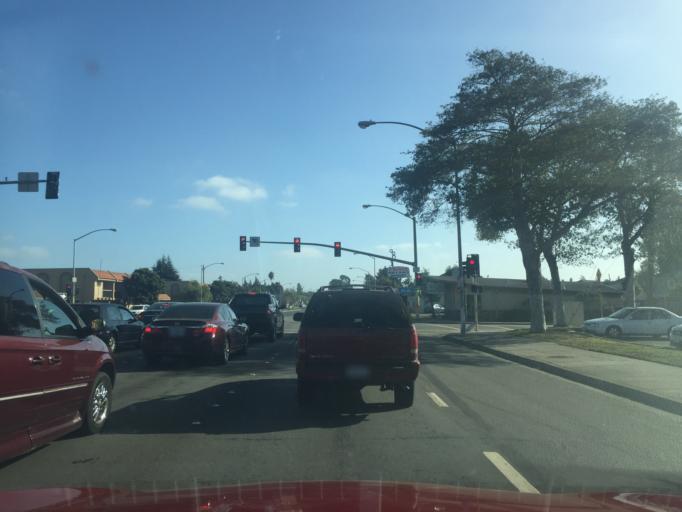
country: US
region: California
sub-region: Alameda County
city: Ashland
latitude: 37.6977
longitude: -122.1301
